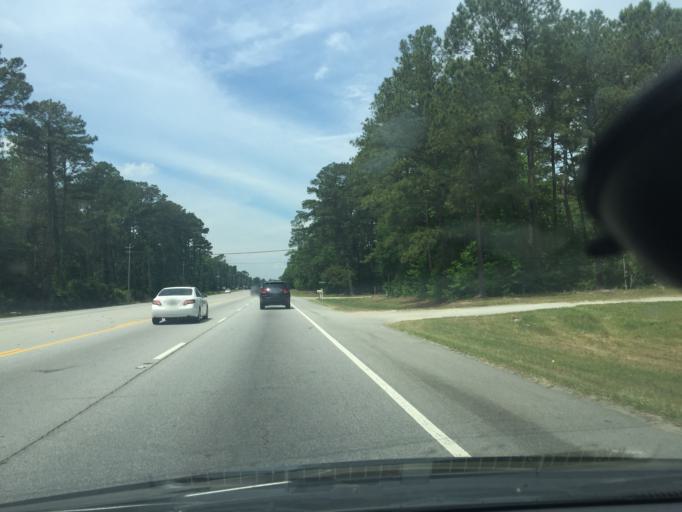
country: US
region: Georgia
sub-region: Chatham County
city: Bloomingdale
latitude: 32.1400
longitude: -81.3226
